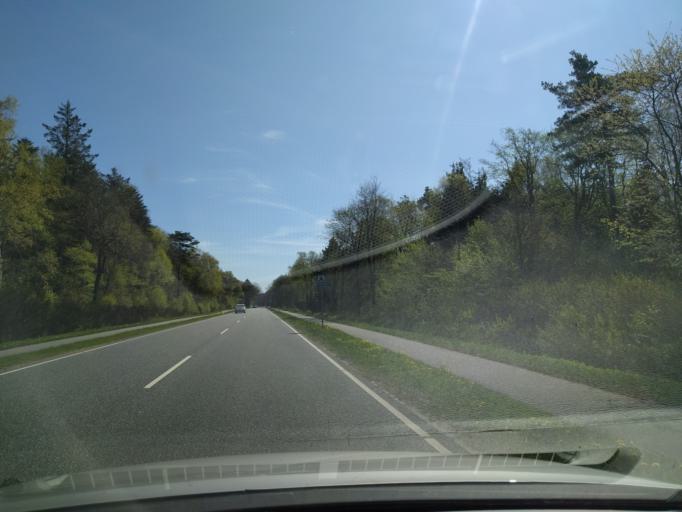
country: DK
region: Central Jutland
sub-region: Ringkobing-Skjern Kommune
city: Ringkobing
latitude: 56.0853
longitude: 8.3103
